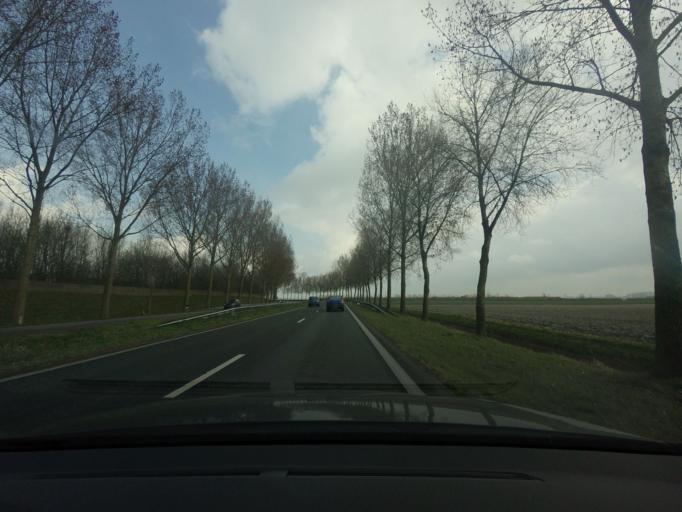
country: NL
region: North Holland
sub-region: Gemeente Haarlemmermeer
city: Hoofddorp
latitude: 52.3026
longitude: 4.7134
